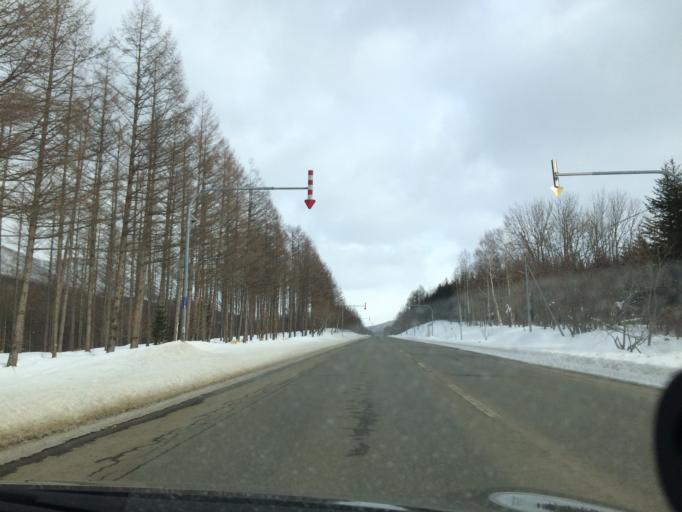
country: JP
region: Hokkaido
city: Shimo-furano
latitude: 43.1314
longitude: 142.6987
